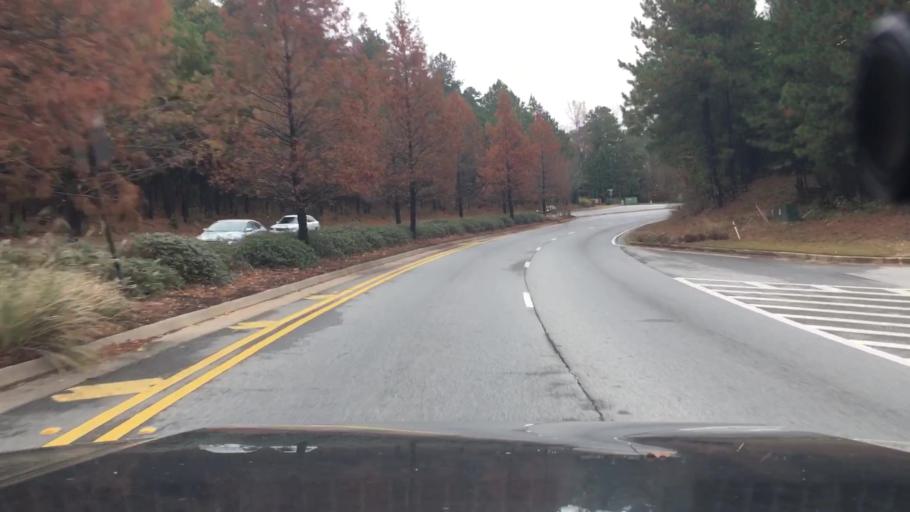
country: US
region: Georgia
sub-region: Coweta County
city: East Newnan
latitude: 33.3748
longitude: -84.7630
